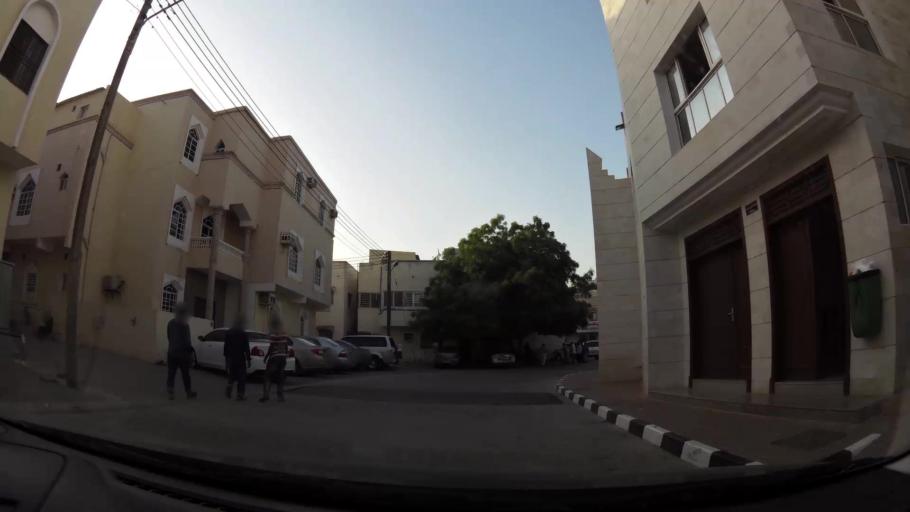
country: OM
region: Zufar
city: Salalah
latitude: 17.0135
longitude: 54.1045
